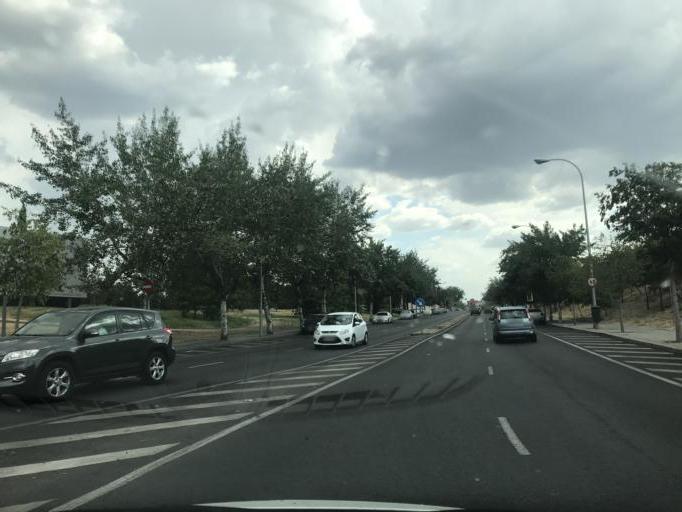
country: ES
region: Madrid
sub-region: Provincia de Madrid
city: Hortaleza
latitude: 40.4808
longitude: -3.6505
